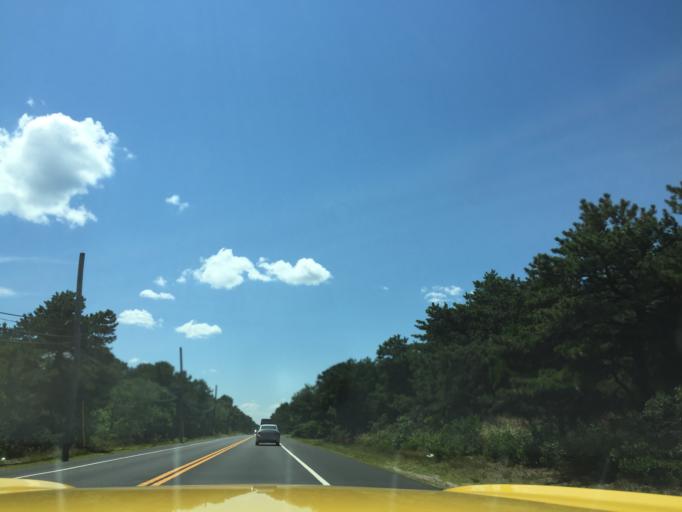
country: US
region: New York
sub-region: Suffolk County
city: Amagansett
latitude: 40.9935
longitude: -72.0629
